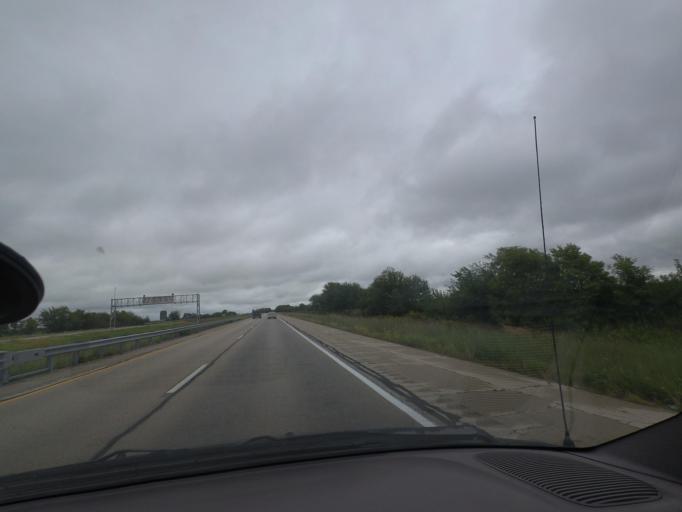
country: US
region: Illinois
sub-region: Piatt County
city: Cerro Gordo
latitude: 40.0183
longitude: -88.7231
